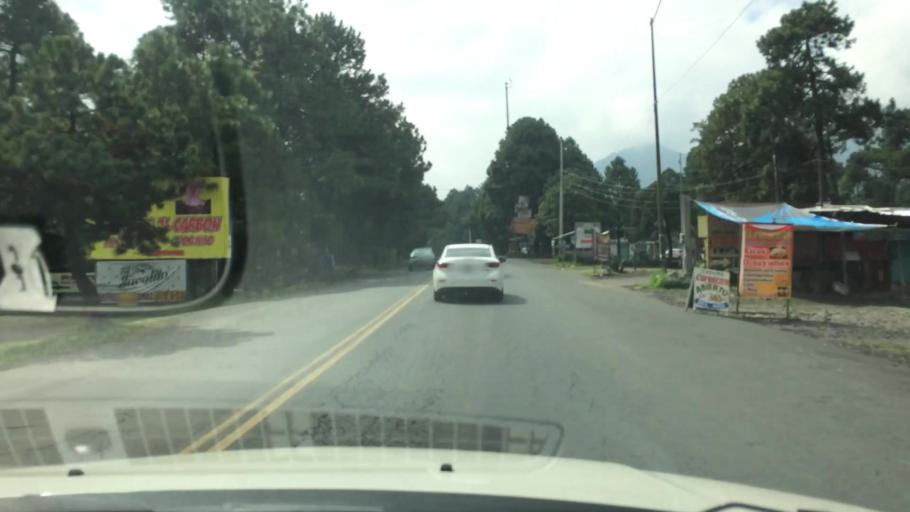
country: MX
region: Mexico City
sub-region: Tlalpan
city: Lomas de Tepemecatl
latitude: 19.2459
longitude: -99.2417
